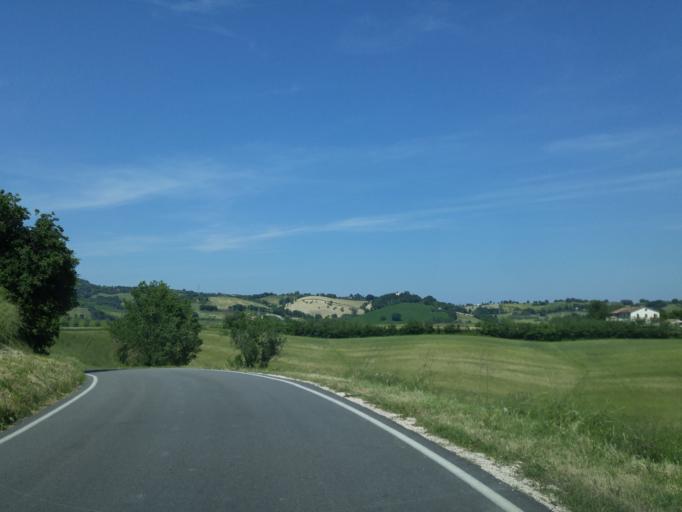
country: IT
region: The Marches
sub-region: Provincia di Pesaro e Urbino
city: Montefelcino
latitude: 43.7307
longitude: 12.8495
